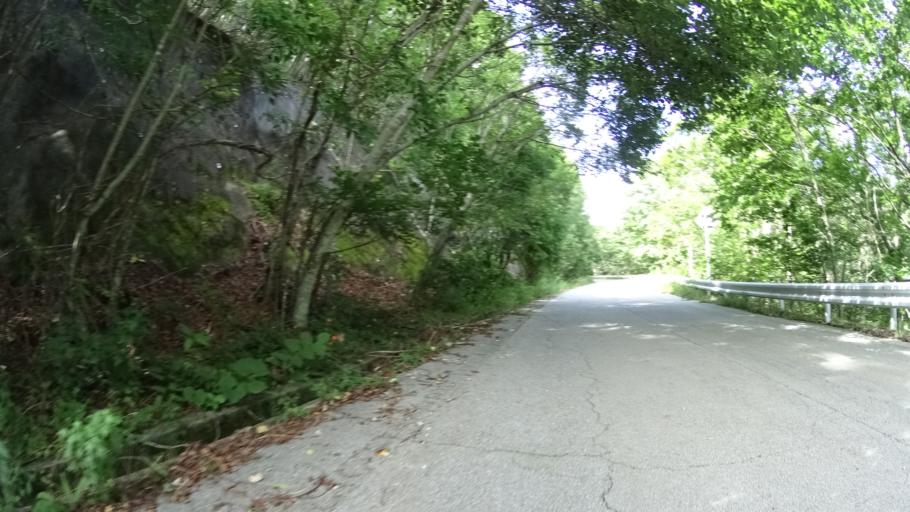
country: JP
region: Yamanashi
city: Nirasaki
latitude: 35.9122
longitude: 138.5417
